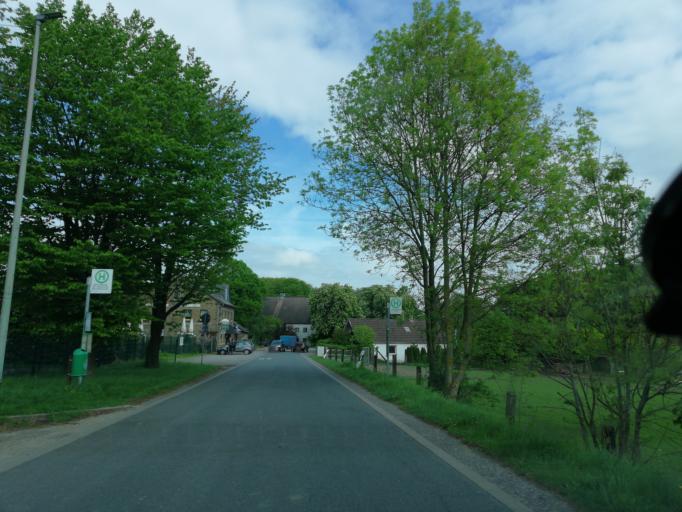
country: DE
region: North Rhine-Westphalia
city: Gevelsberg
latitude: 51.3551
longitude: 7.2992
